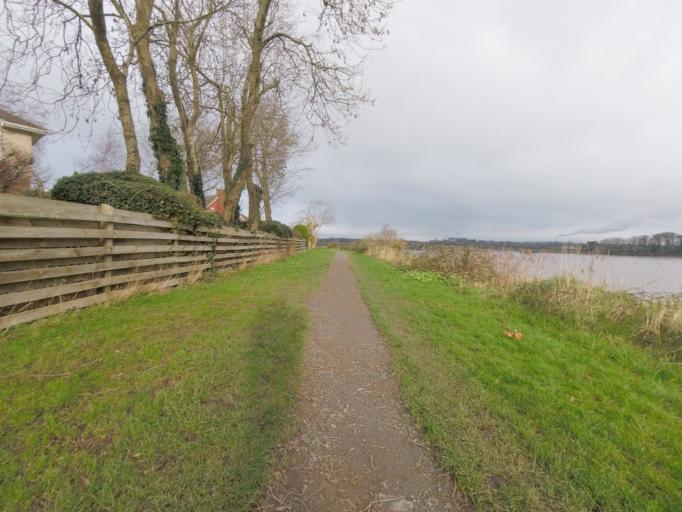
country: IE
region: Munster
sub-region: Waterford
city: Waterford
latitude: 52.2518
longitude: -7.0678
